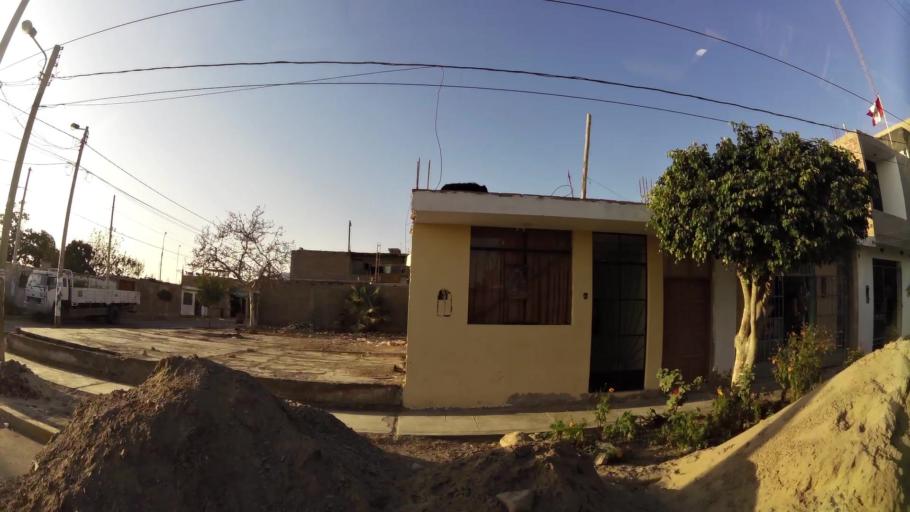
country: PE
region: Ica
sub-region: Provincia de Pisco
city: Villa Tupac Amaru
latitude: -13.7126
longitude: -76.1500
